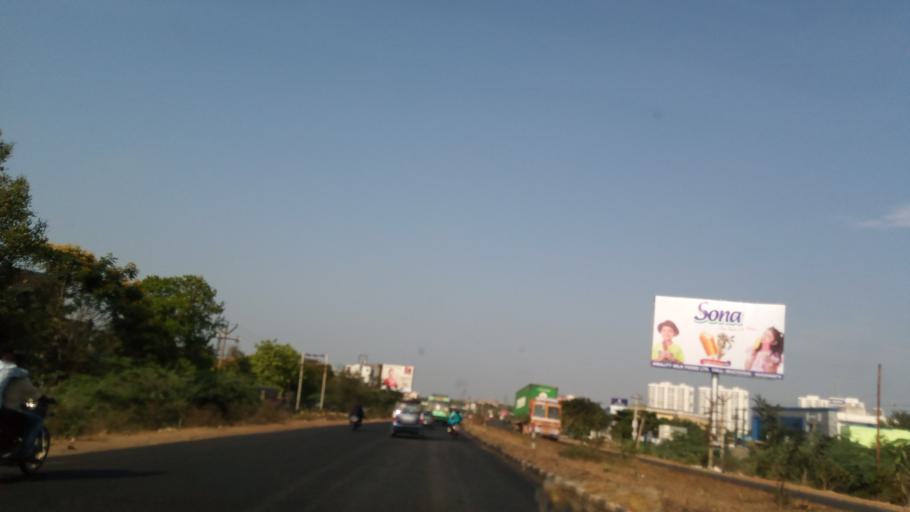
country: IN
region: Tamil Nadu
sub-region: Kancheepuram
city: Nandambakkam
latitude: 13.0350
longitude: 80.0413
